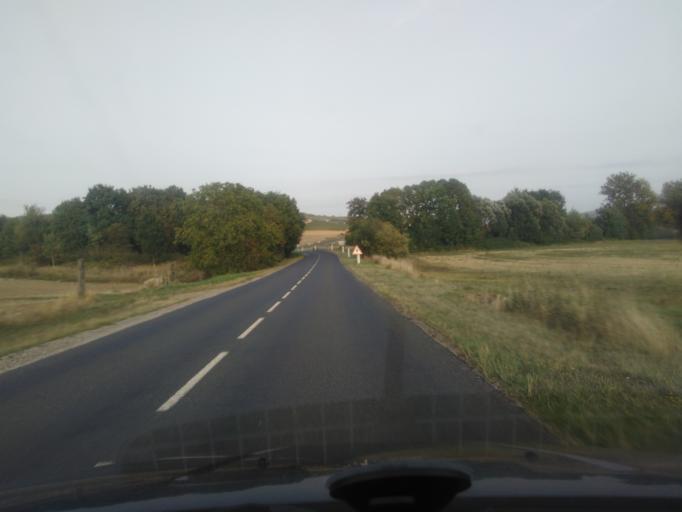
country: FR
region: Champagne-Ardenne
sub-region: Departement de la Marne
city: Mareuil-le-Port
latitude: 49.0883
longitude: 3.7768
